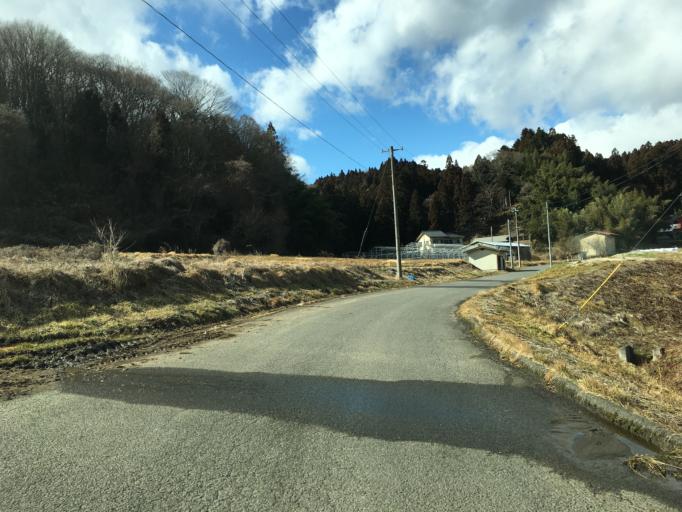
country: JP
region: Fukushima
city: Ishikawa
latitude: 37.2401
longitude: 140.5866
